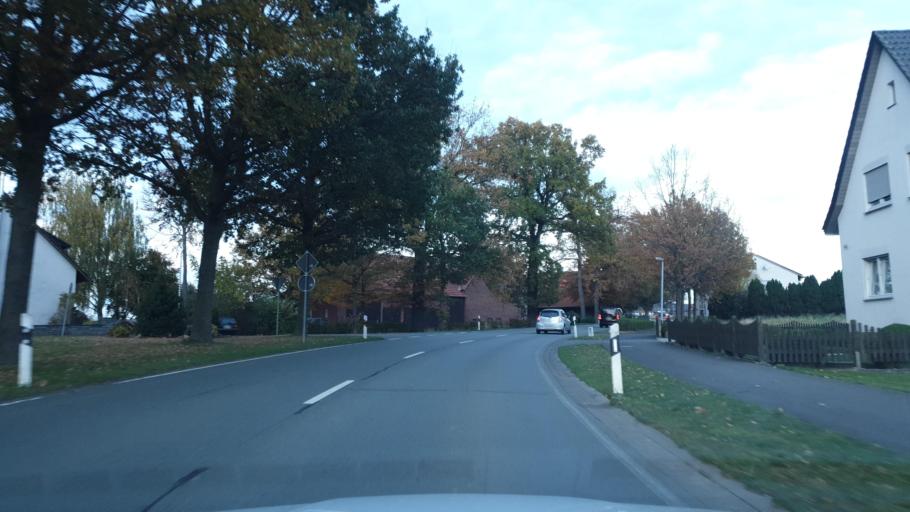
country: DE
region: North Rhine-Westphalia
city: Spenge
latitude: 52.1592
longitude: 8.4982
